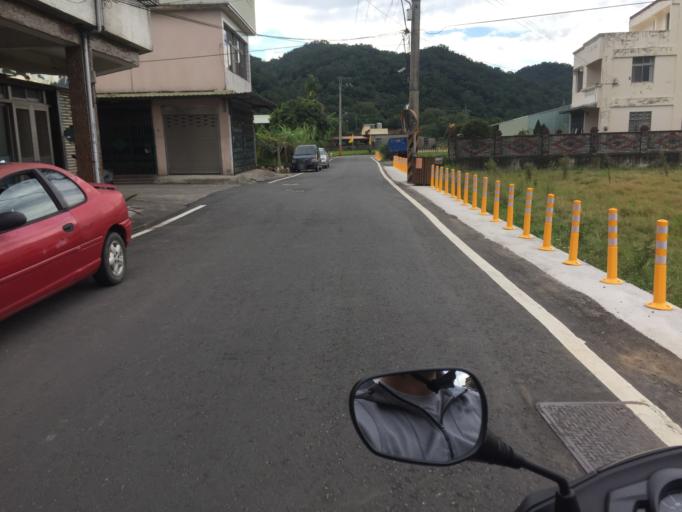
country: TW
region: Taiwan
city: Daxi
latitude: 24.7885
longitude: 121.1752
